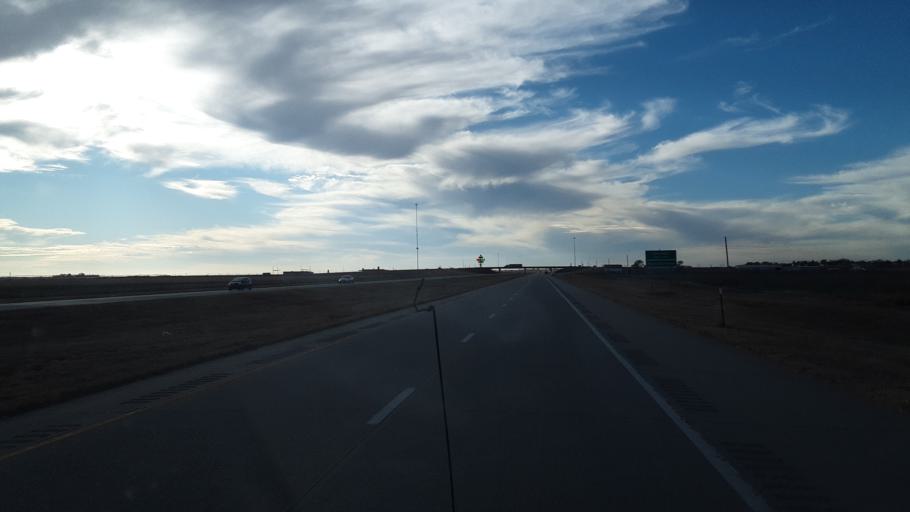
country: US
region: Kansas
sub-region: Finney County
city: Holcomb
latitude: 38.0034
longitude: -100.9840
